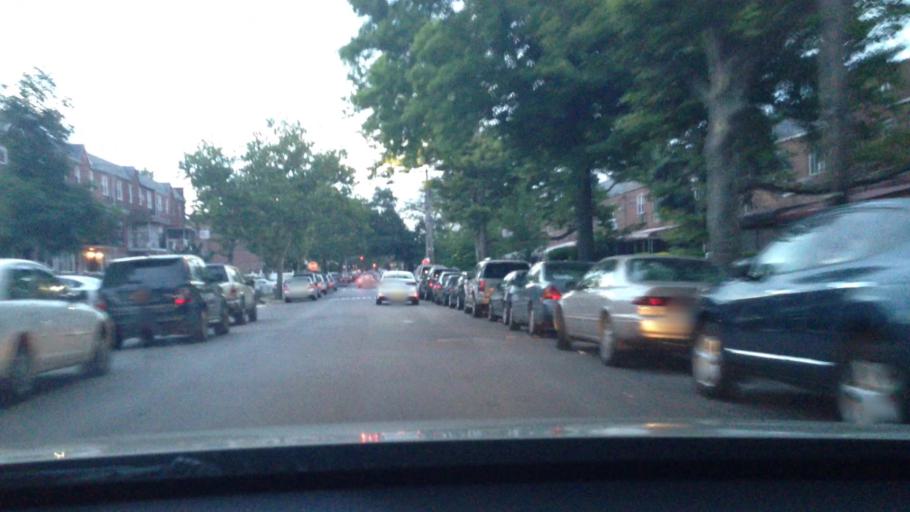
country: US
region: New York
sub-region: Kings County
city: East New York
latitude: 40.6324
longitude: -73.9073
